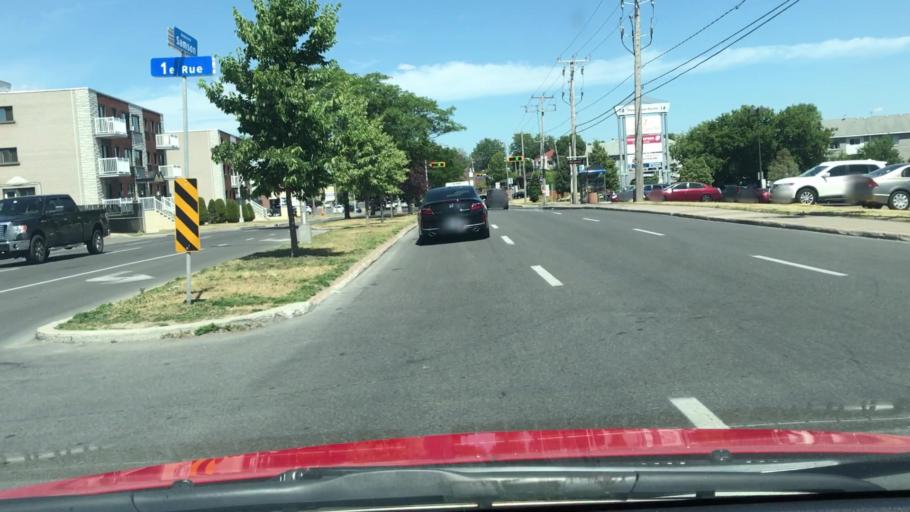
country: CA
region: Quebec
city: Dollard-Des Ormeaux
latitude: 45.5288
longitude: -73.7574
